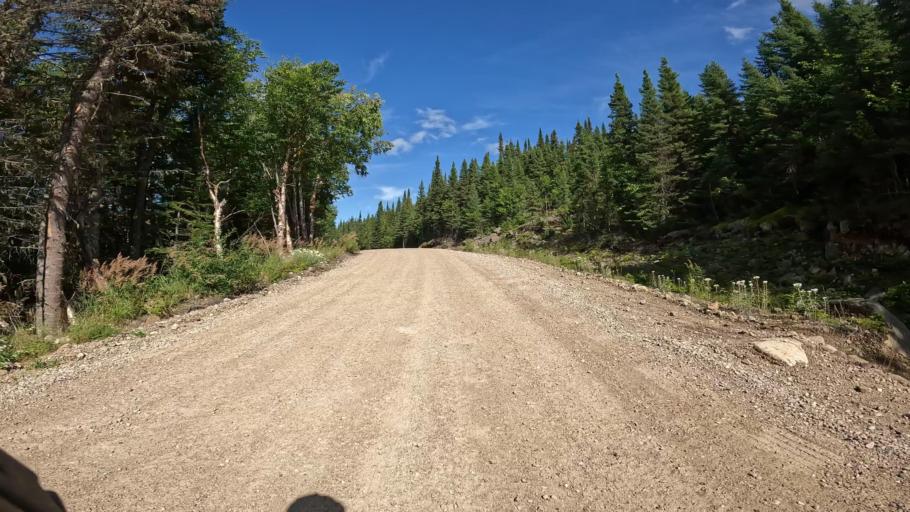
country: CA
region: Quebec
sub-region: Capitale-Nationale
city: Baie-Saint-Paul
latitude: 47.8043
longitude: -70.6774
